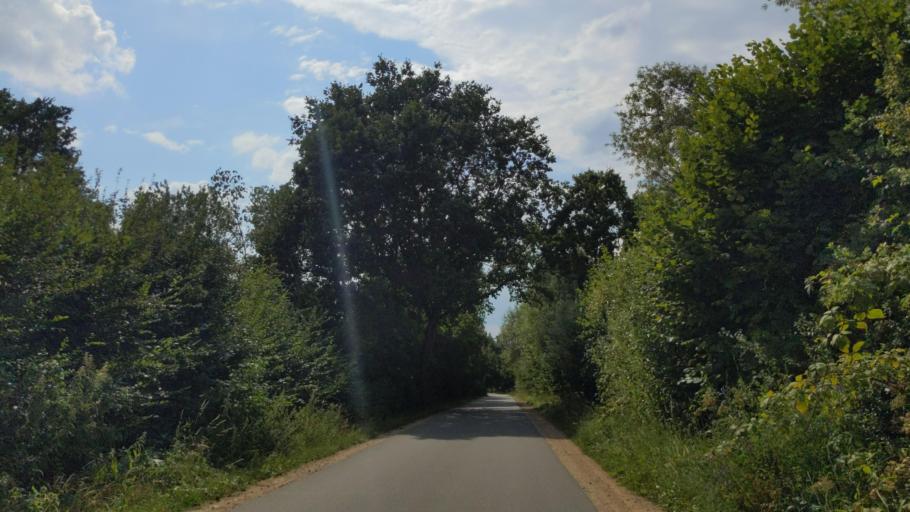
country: DE
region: Mecklenburg-Vorpommern
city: Selmsdorf
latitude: 53.8413
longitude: 10.8857
